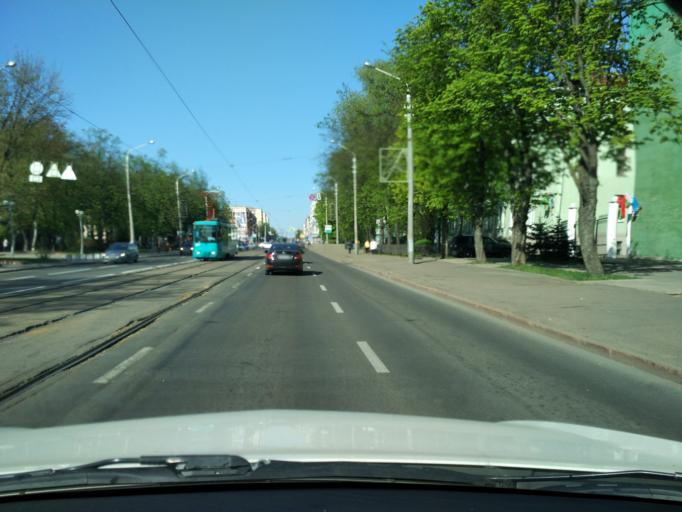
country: BY
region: Minsk
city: Minsk
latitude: 53.9236
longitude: 27.5913
